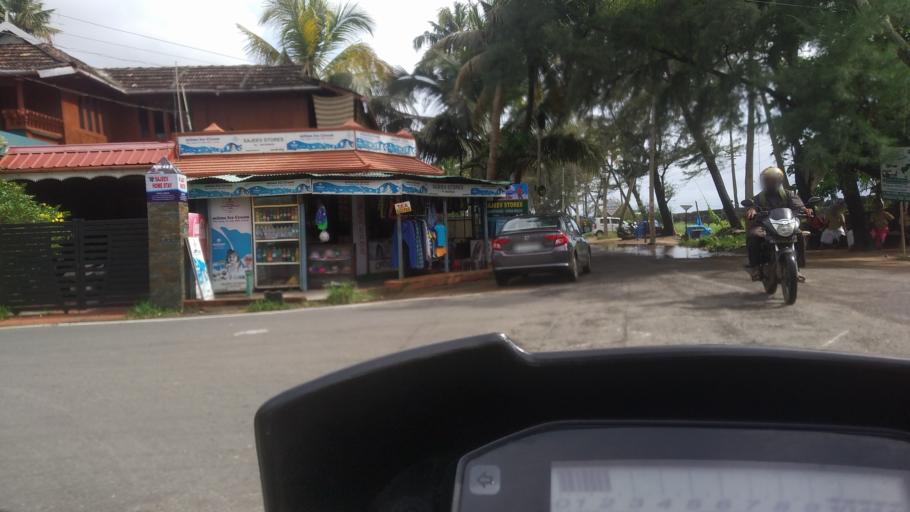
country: IN
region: Kerala
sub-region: Thrissur District
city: Kodungallur
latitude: 10.1392
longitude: 76.1794
